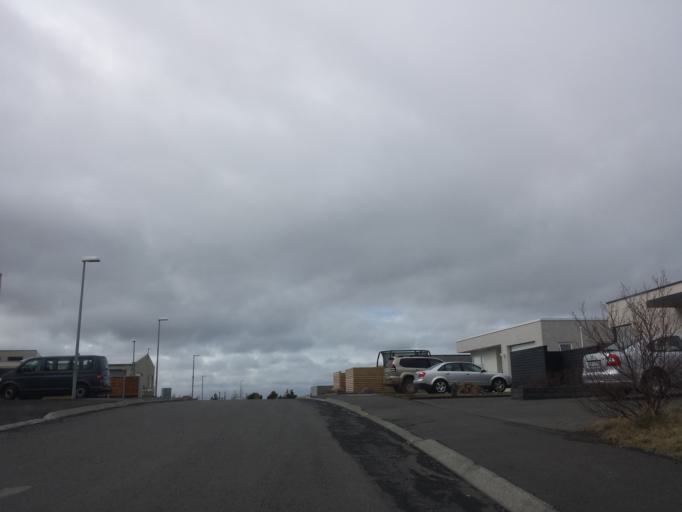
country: IS
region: Capital Region
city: Kopavogur
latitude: 64.0883
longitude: -21.8612
